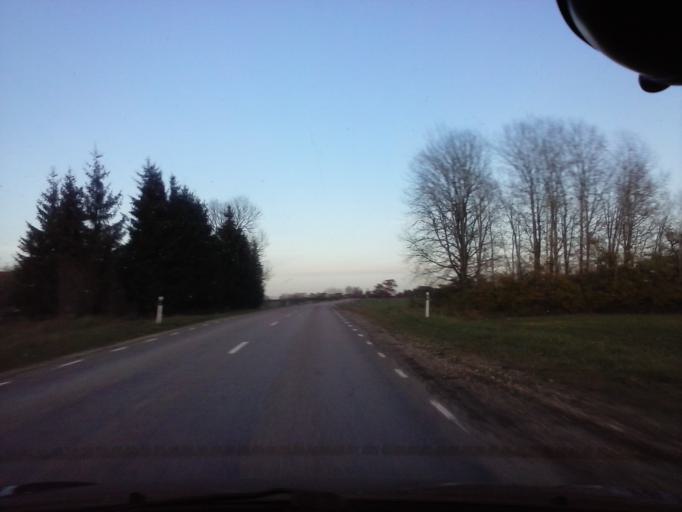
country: EE
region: Harju
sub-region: Nissi vald
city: Turba
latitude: 58.9058
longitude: 24.1188
